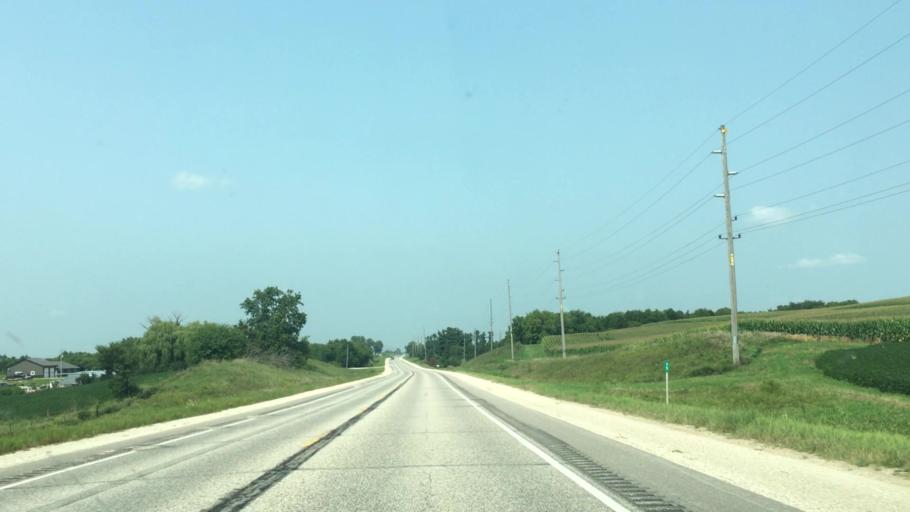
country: US
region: Iowa
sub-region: Fayette County
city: Fayette
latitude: 42.8722
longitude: -91.8105
